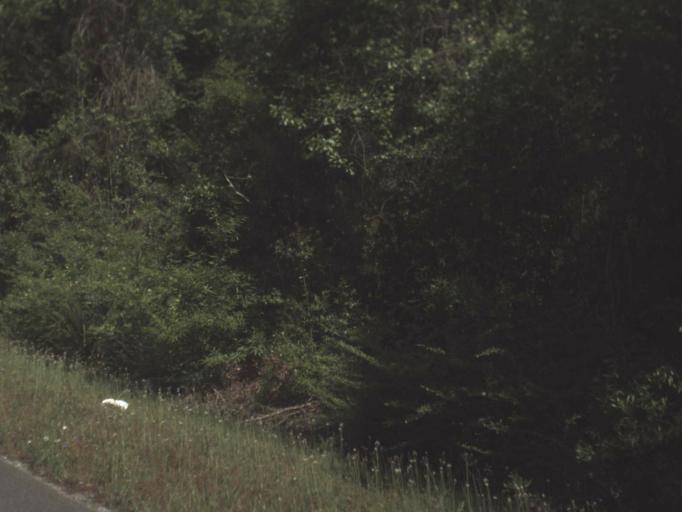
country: US
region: Florida
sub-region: Escambia County
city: Myrtle Grove
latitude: 30.4152
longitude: -87.3630
